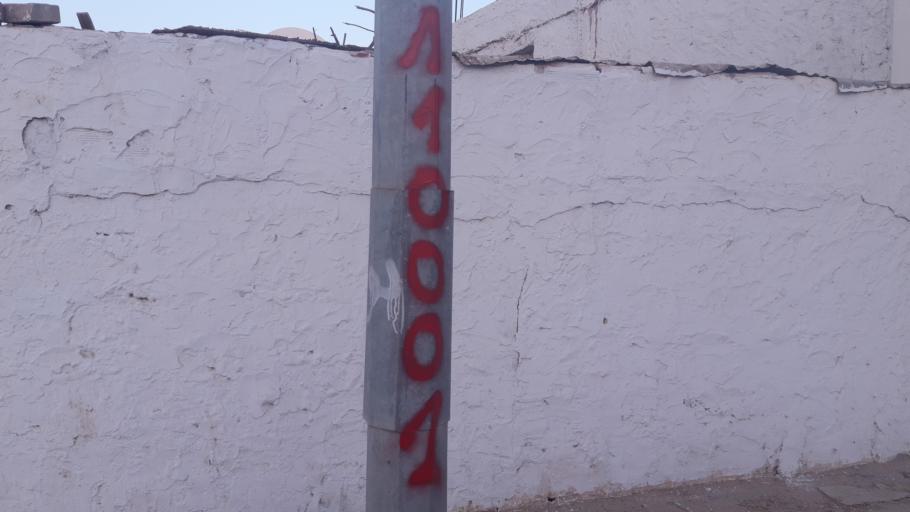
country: TN
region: Madanin
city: Zarzis
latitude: 33.5240
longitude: 11.1110
